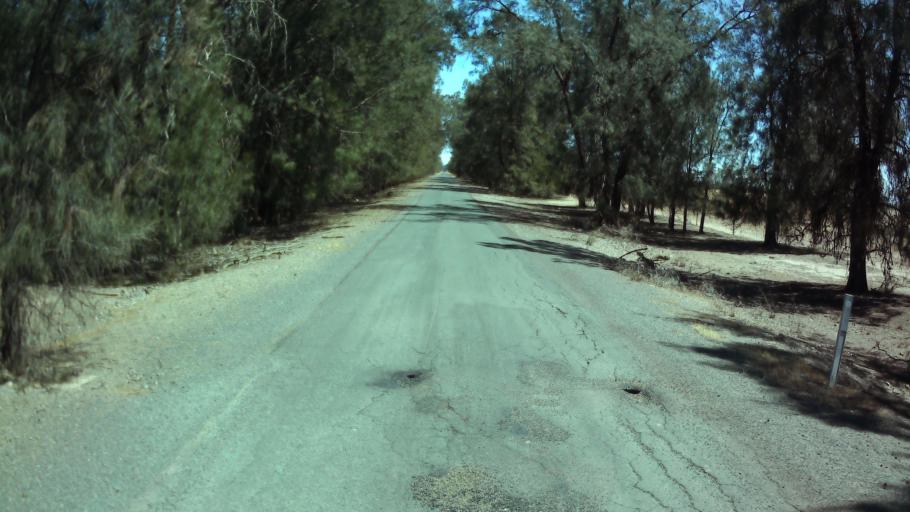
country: AU
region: New South Wales
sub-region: Weddin
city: Grenfell
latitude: -33.8826
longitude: 147.6897
